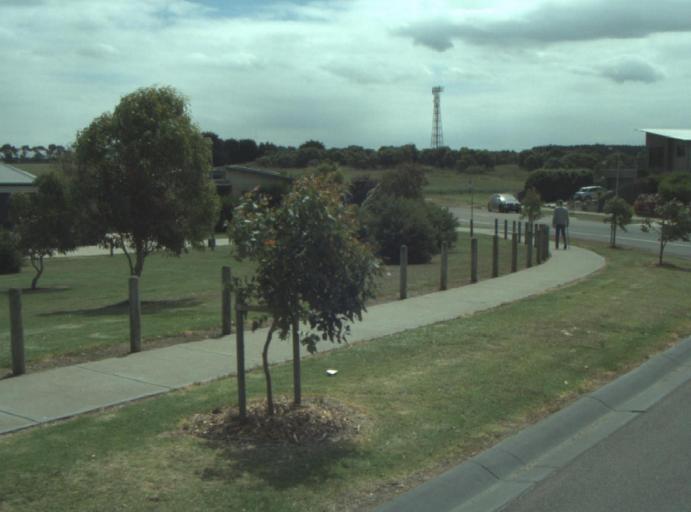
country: AU
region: Victoria
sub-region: Greater Geelong
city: Clifton Springs
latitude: -38.2535
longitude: 144.5468
